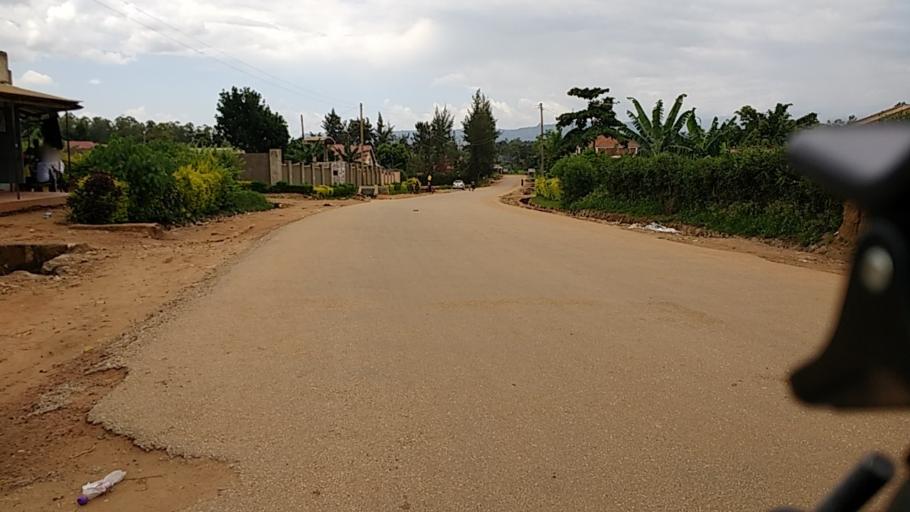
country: UG
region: Eastern Region
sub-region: Mbale District
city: Mbale
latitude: 1.0844
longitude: 34.1724
